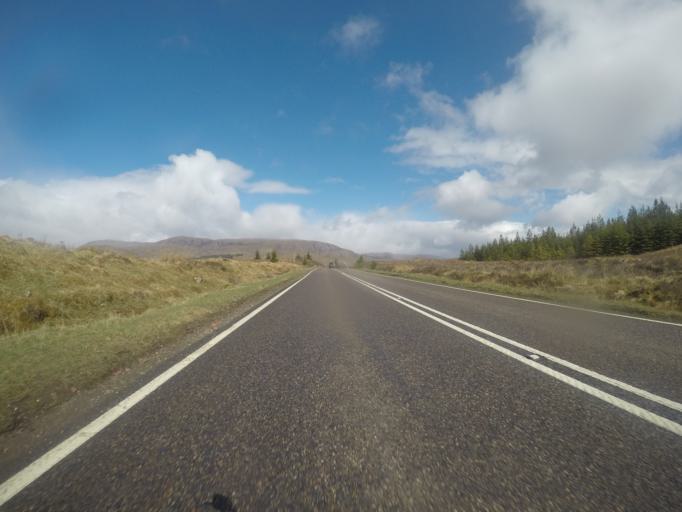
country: GB
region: Scotland
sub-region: Highland
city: Spean Bridge
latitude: 57.0952
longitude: -4.9944
